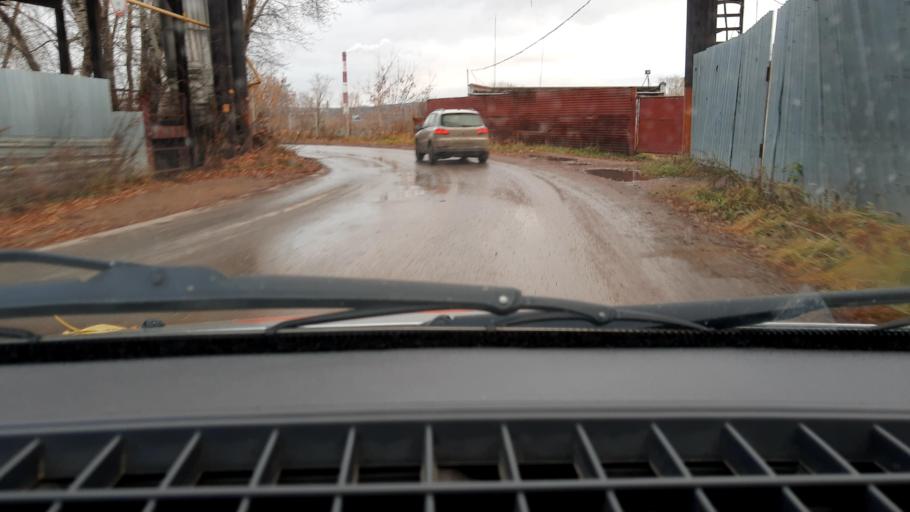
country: RU
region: Bashkortostan
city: Ufa
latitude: 54.8346
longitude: 56.1167
